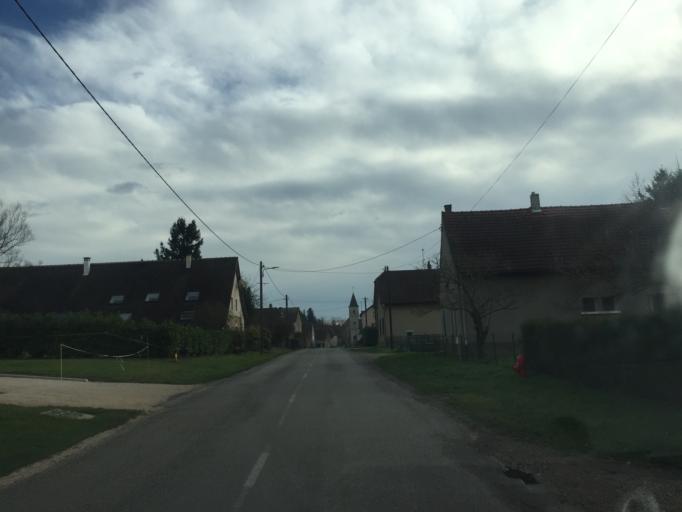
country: FR
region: Franche-Comte
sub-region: Departement du Jura
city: Chaussin
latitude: 46.9172
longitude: 5.4536
